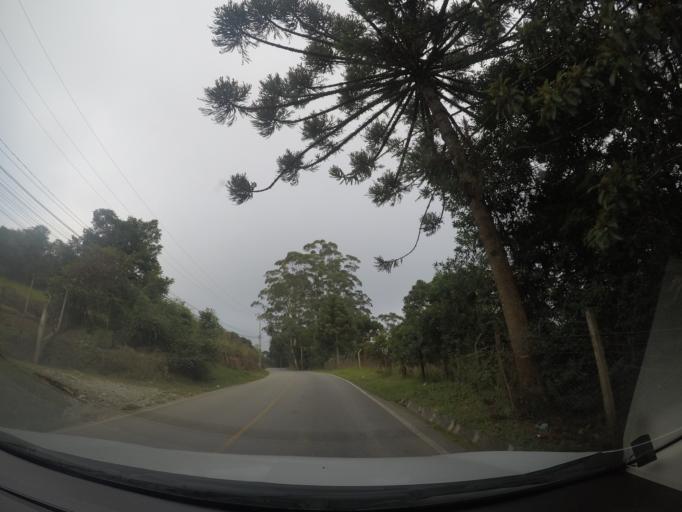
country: BR
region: Parana
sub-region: Colombo
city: Colombo
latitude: -25.2953
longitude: -49.2284
